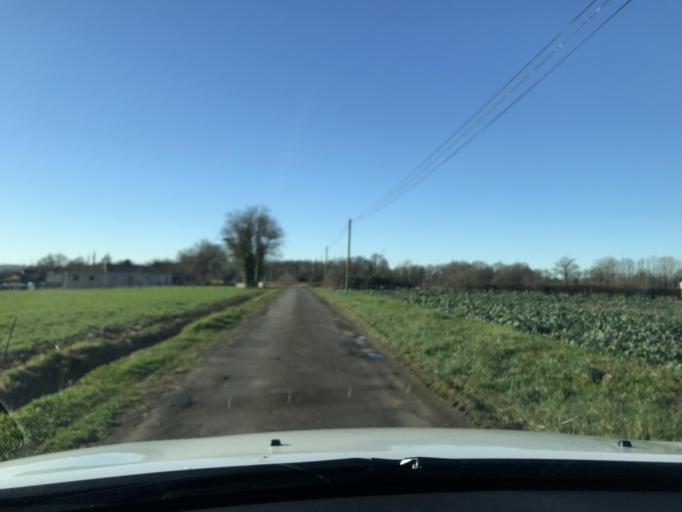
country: FR
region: Poitou-Charentes
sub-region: Departement de la Charente
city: Loubert
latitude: 45.8425
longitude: 0.5391
